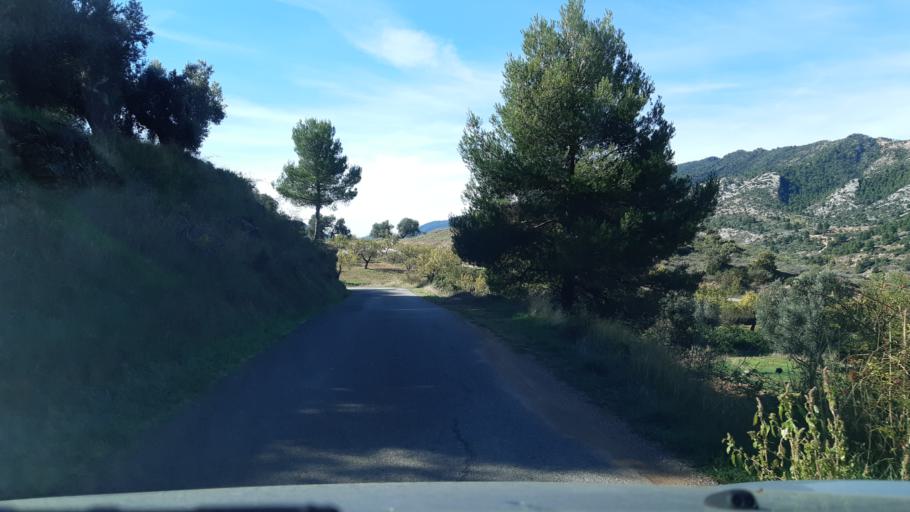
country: ES
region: Aragon
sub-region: Provincia de Teruel
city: Valderrobres
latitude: 40.8351
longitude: 0.1912
